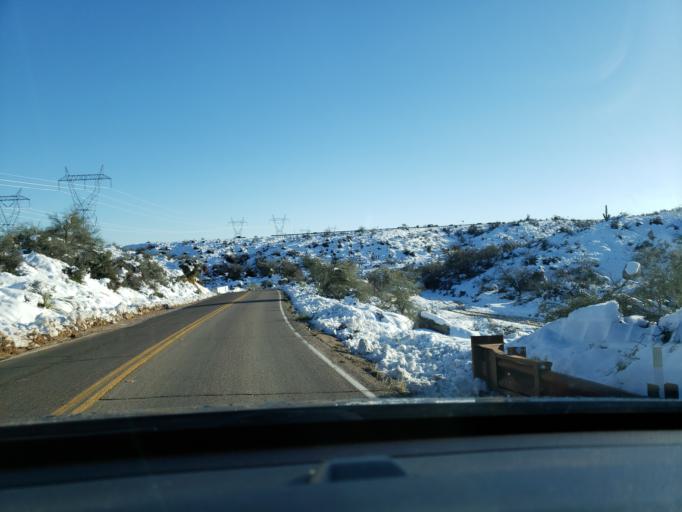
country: US
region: Arizona
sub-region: Maricopa County
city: Carefree
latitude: 33.8796
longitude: -111.8159
